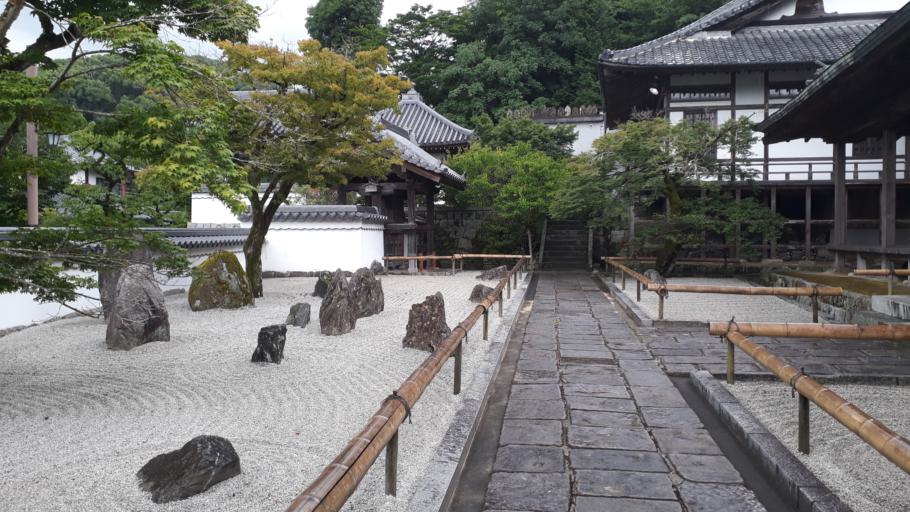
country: JP
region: Fukuoka
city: Dazaifu
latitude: 33.5189
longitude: 130.5336
